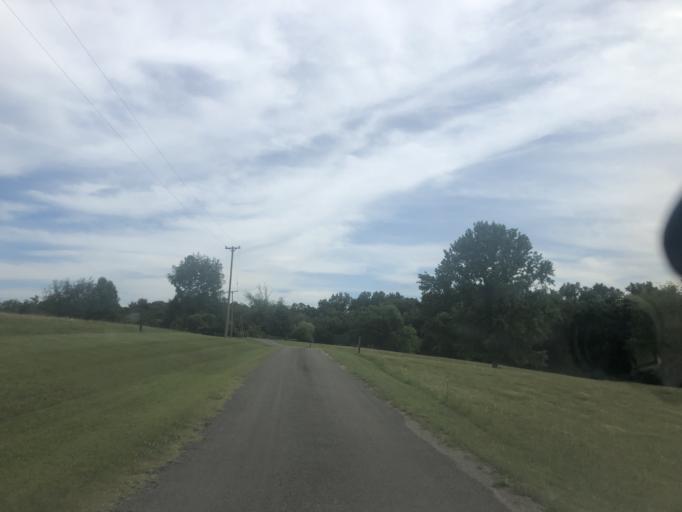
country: US
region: Tennessee
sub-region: Davidson County
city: Lakewood
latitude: 36.2162
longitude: -86.6623
